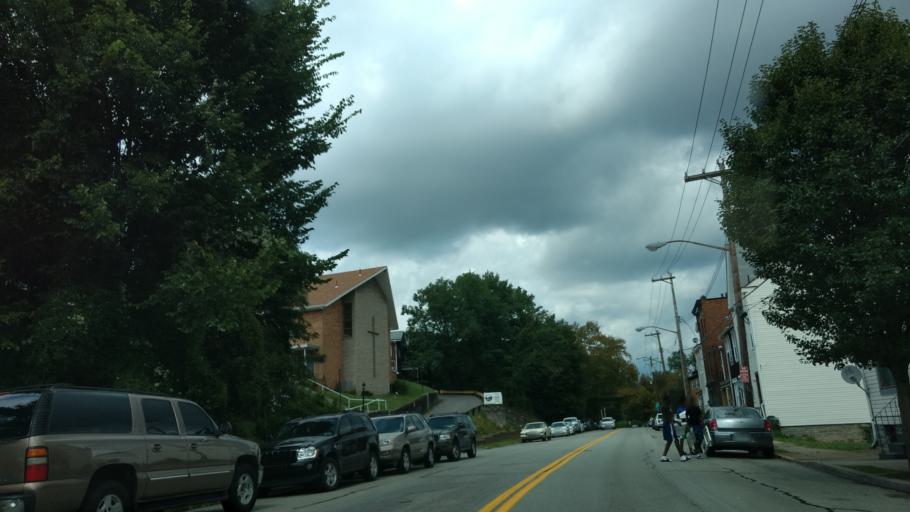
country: US
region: Pennsylvania
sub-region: Allegheny County
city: Millvale
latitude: 40.4765
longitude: -80.0124
